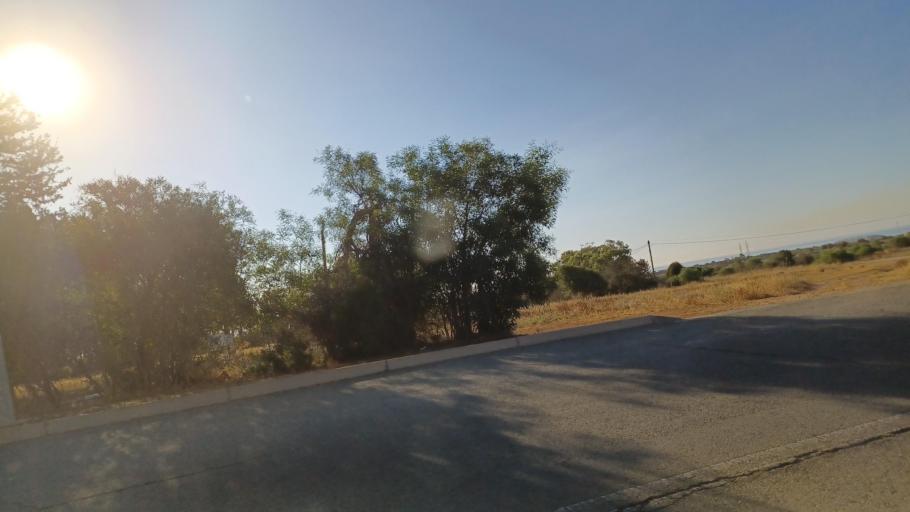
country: CY
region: Larnaka
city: Xylotymbou
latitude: 34.9996
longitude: 33.7426
